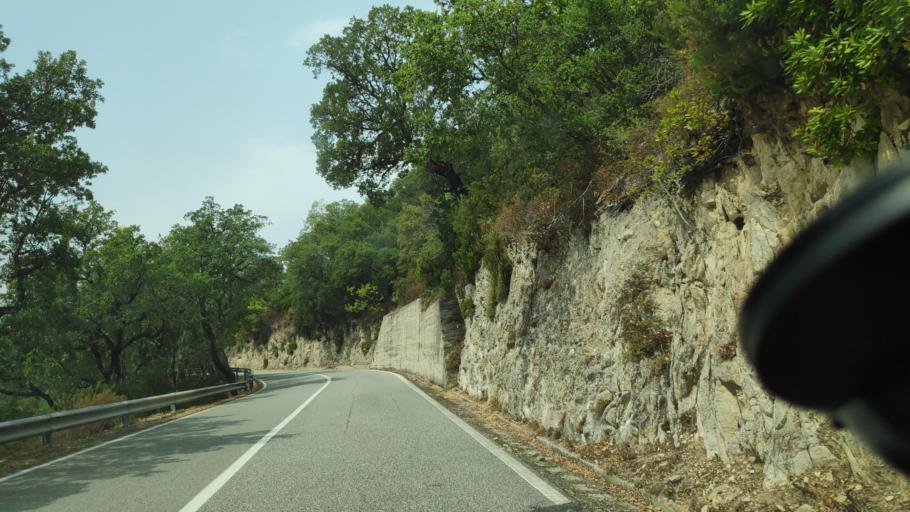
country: IT
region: Calabria
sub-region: Provincia di Catanzaro
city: San Sostene
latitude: 38.6371
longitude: 16.5102
